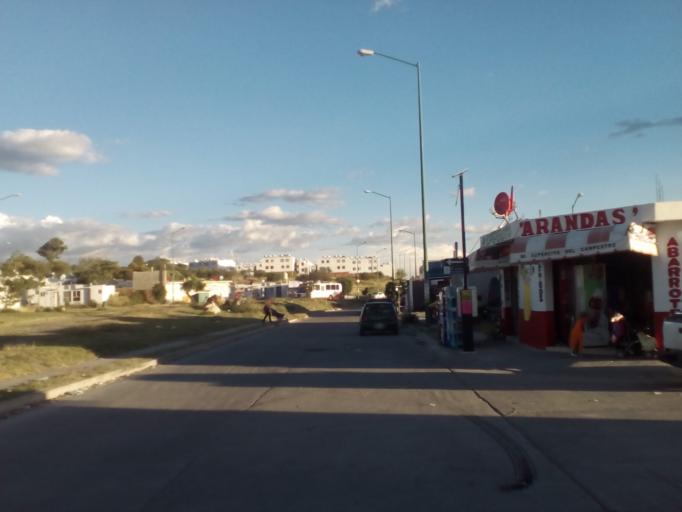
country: MX
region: Guanajuato
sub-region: Leon
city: Fraccionamiento Paseo de las Torres
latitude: 21.1901
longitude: -101.7655
